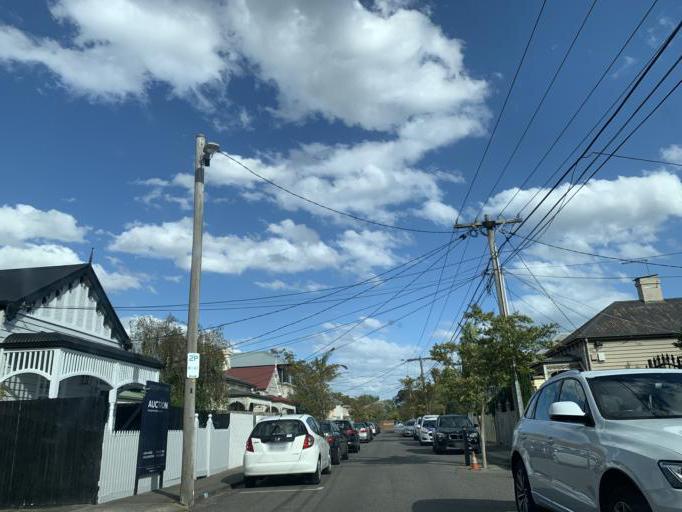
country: AU
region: Victoria
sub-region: Bayside
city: North Brighton
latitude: -37.9146
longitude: 144.9994
